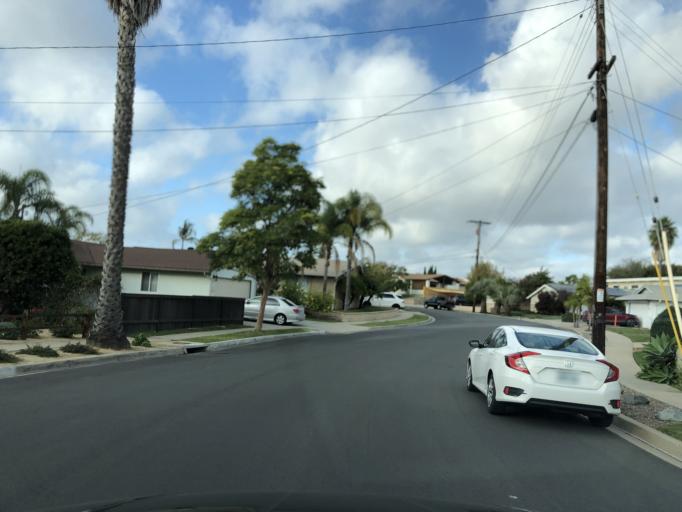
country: US
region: California
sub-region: San Diego County
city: La Jolla
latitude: 32.8182
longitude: -117.1890
